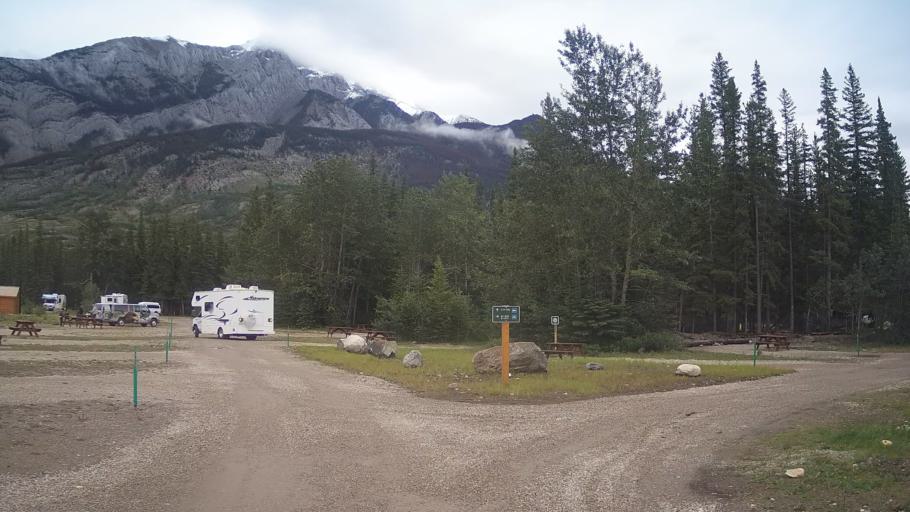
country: CA
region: Alberta
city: Jasper Park Lodge
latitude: 53.0149
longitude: -118.0837
